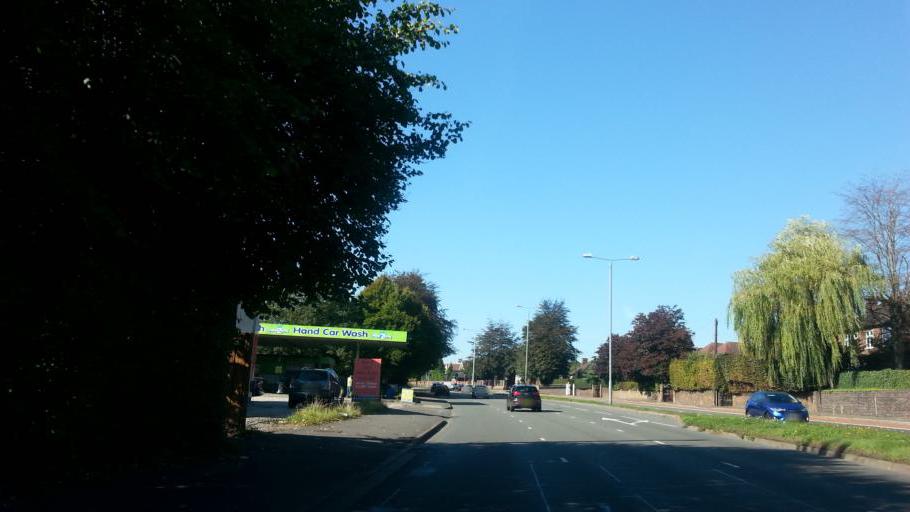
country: GB
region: England
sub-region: Derbyshire
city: Long Eaton
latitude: 52.9379
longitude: -1.2382
